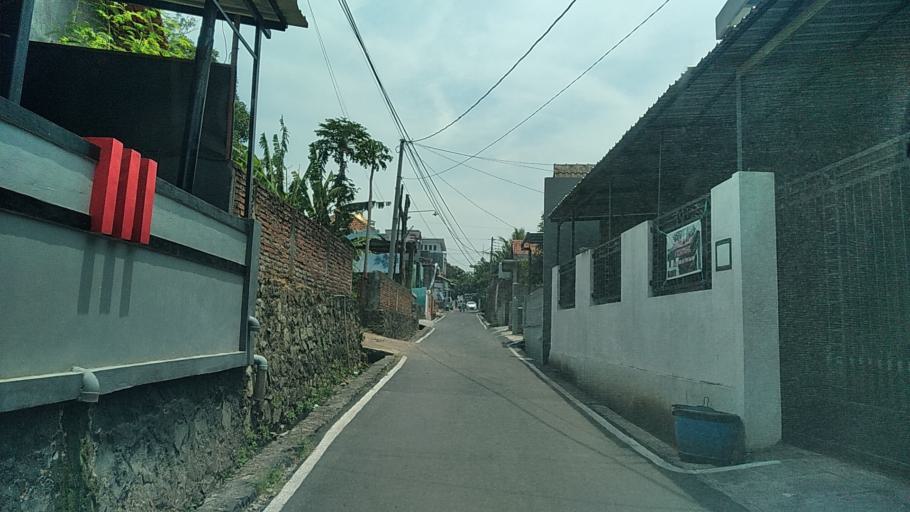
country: ID
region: Central Java
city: Semarang
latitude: -7.0562
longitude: 110.4228
